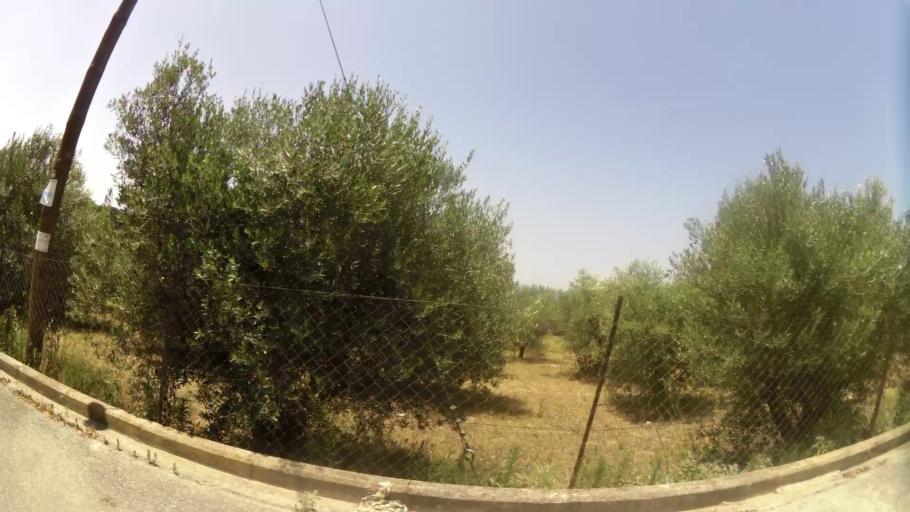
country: GR
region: Central Macedonia
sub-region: Nomos Thessalonikis
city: Trilofos
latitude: 40.4759
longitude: 22.9710
